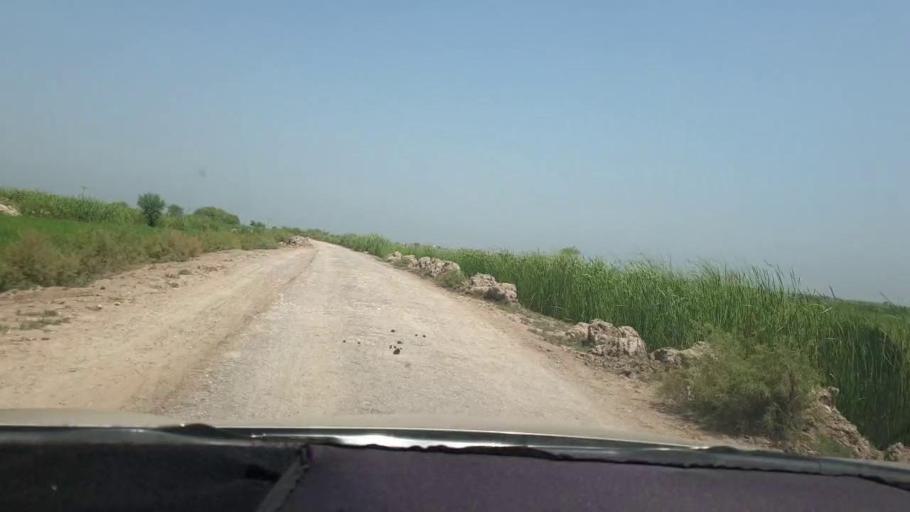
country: PK
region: Sindh
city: Shahdadkot
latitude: 27.8330
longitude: 67.9932
